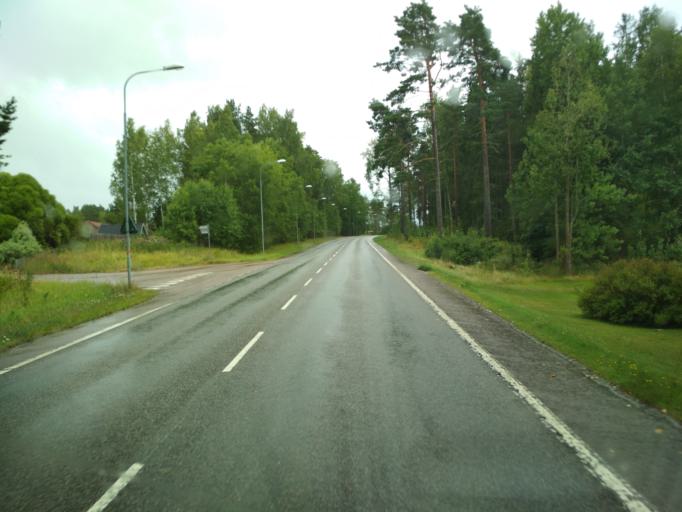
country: SE
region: Vaestmanland
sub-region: Surahammars Kommun
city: Ramnas
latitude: 59.7707
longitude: 16.2011
